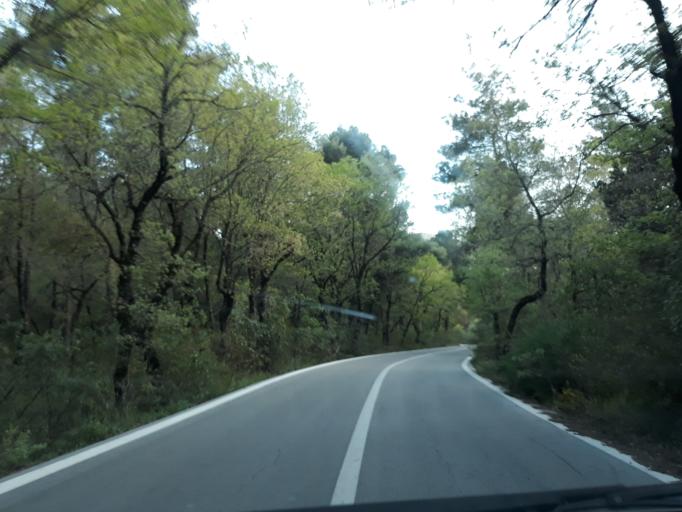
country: GR
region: Attica
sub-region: Nomarchia Anatolikis Attikis
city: Afidnes
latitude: 38.1995
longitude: 23.7860
